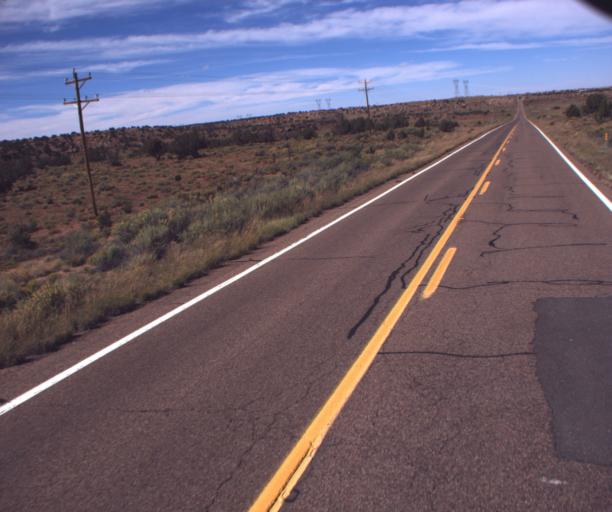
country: US
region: Arizona
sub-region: Apache County
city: Saint Johns
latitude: 34.5398
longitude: -109.6213
